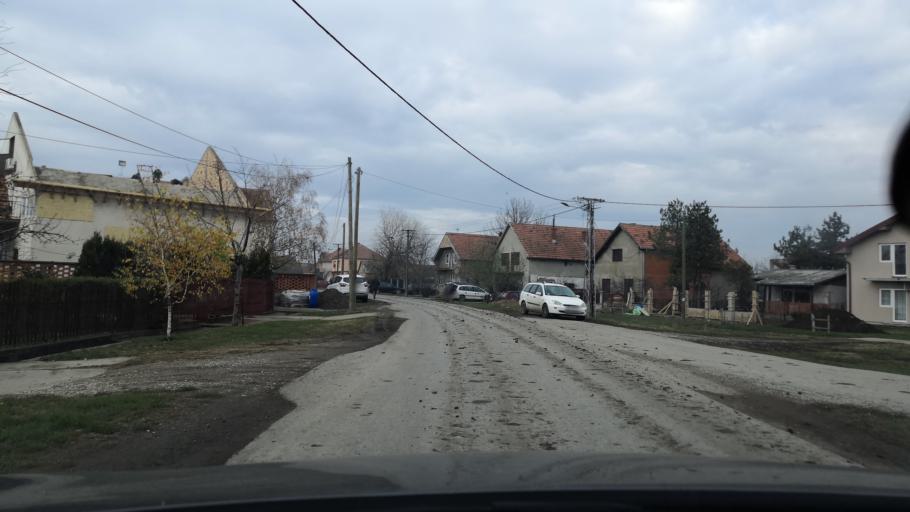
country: RS
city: Ugrinovci
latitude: 44.8870
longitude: 20.1465
